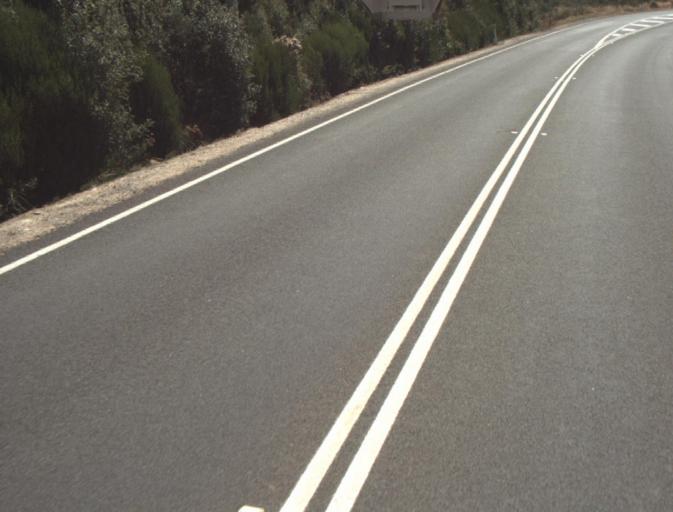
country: AU
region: Tasmania
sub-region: Launceston
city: Mayfield
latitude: -41.3613
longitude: 147.1435
